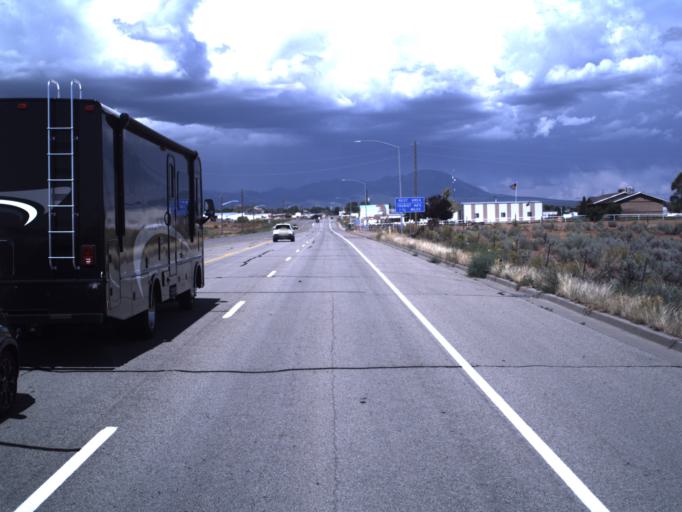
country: US
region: Utah
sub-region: San Juan County
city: Blanding
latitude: 37.6043
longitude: -109.4787
